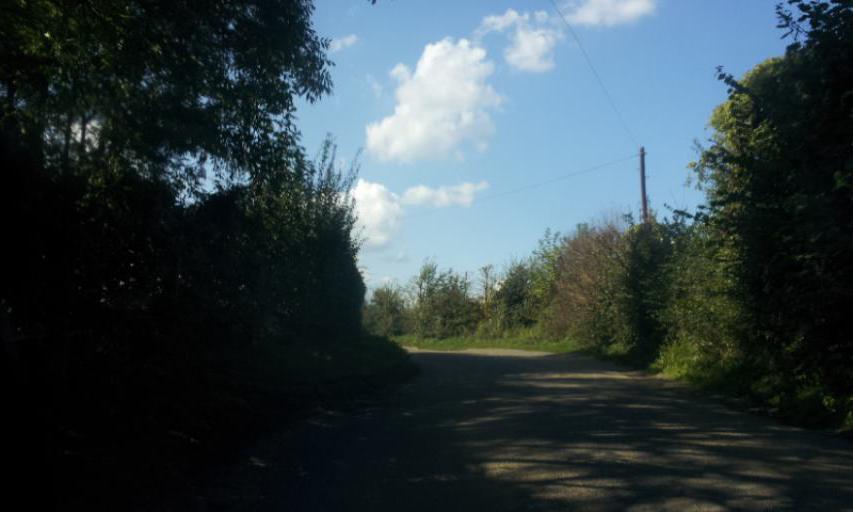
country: GB
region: England
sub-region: Kent
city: Hadlow
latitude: 51.2196
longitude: 0.3613
